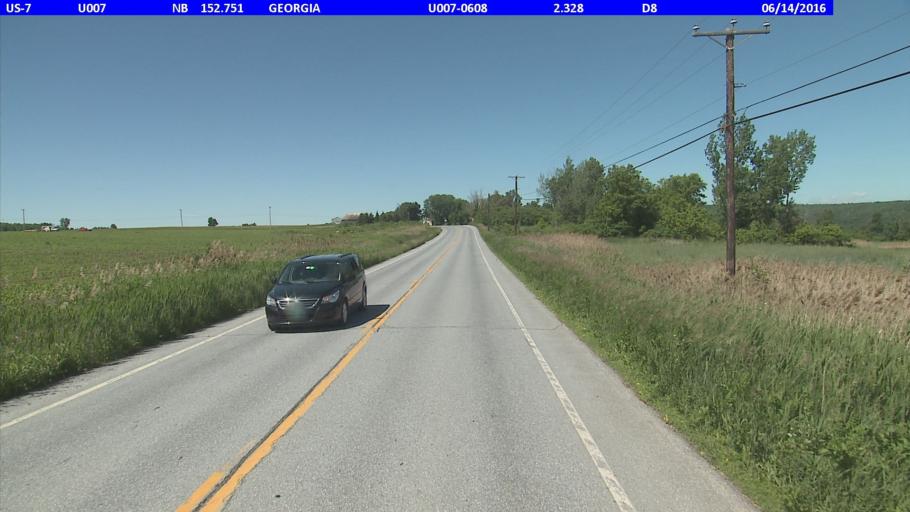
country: US
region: Vermont
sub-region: Chittenden County
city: Milton
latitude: 44.7121
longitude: -73.1019
